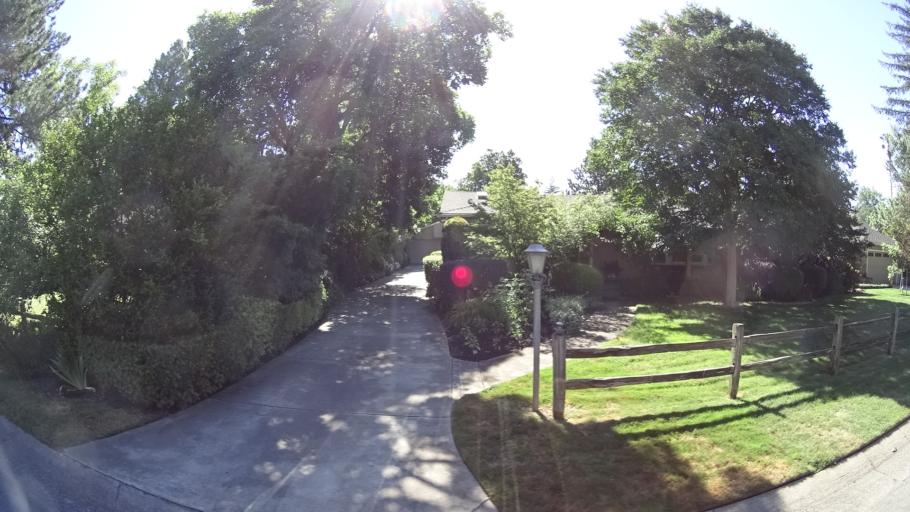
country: US
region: California
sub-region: Sacramento County
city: Sacramento
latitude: 38.5353
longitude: -121.5008
